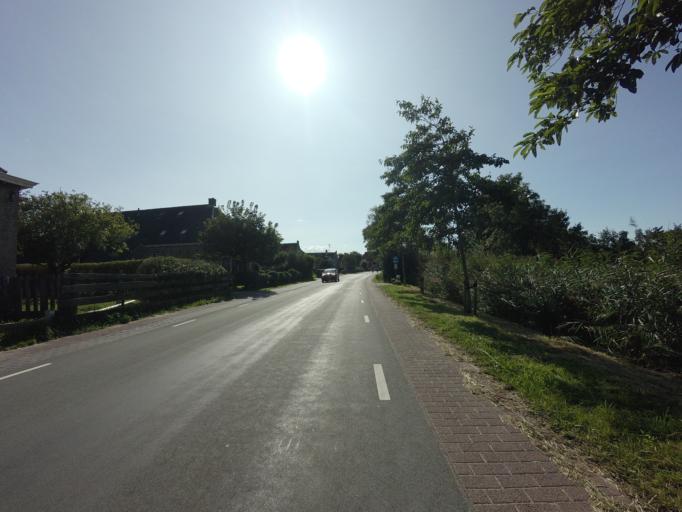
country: NL
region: Friesland
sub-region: Gemeente Terschelling
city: West-Terschelling
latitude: 53.3946
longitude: 5.3294
